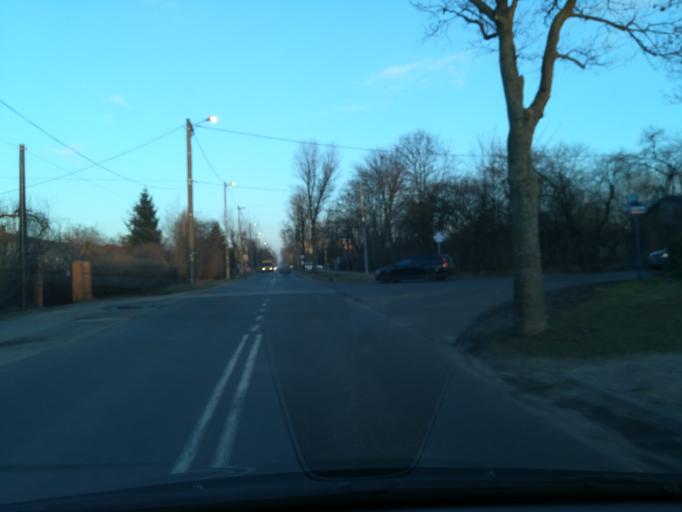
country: PL
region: Lodz Voivodeship
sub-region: Piotrkow Trybunalski
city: Piotrkow Trybunalski
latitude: 51.4112
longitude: 19.6472
